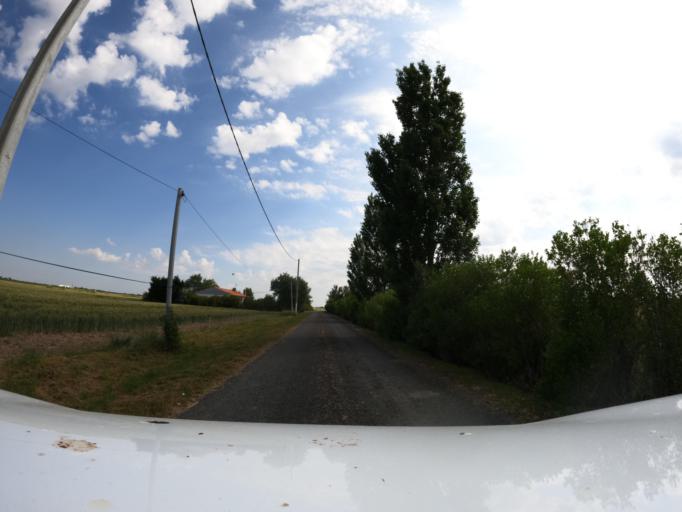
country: FR
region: Poitou-Charentes
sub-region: Departement de la Charente-Maritime
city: Charron
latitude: 46.3314
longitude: -1.1190
